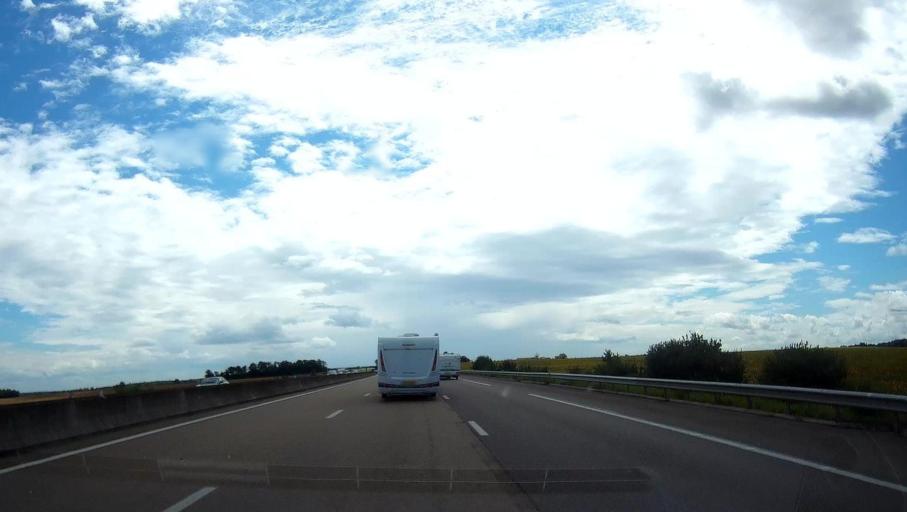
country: FR
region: Bourgogne
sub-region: Departement de la Cote-d'Or
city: Marcilly-sur-Tille
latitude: 47.4993
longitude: 5.1901
